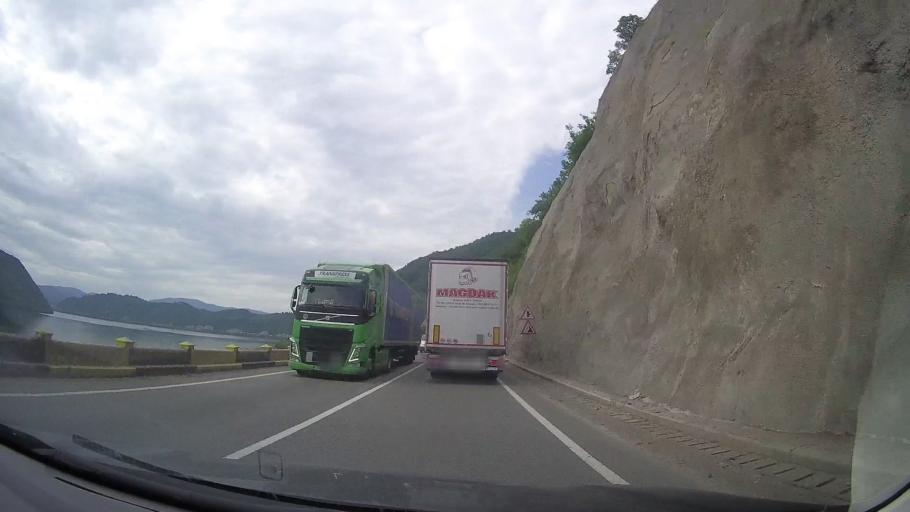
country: RO
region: Mehedinti
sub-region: Comuna Ilovita
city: Ilovita
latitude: 44.7056
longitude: 22.4929
